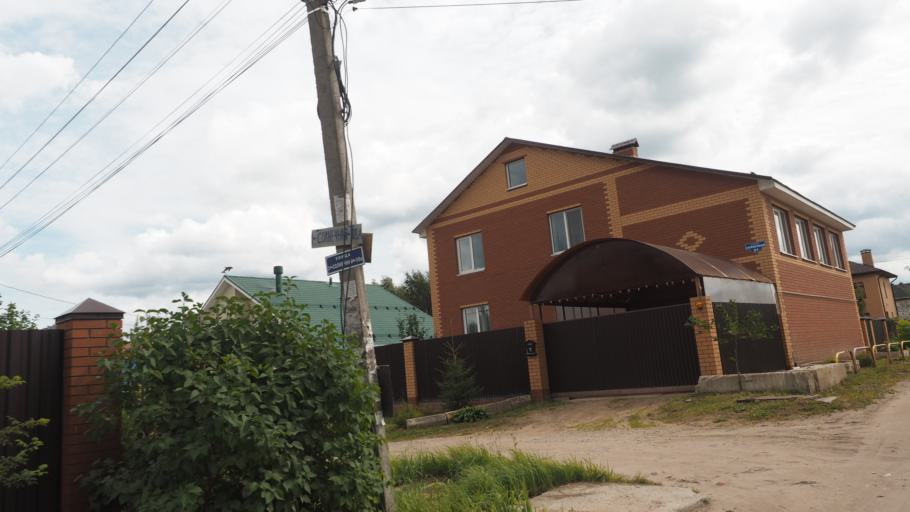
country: RU
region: Moskovskaya
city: Ramenskoye
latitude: 55.5702
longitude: 38.2778
